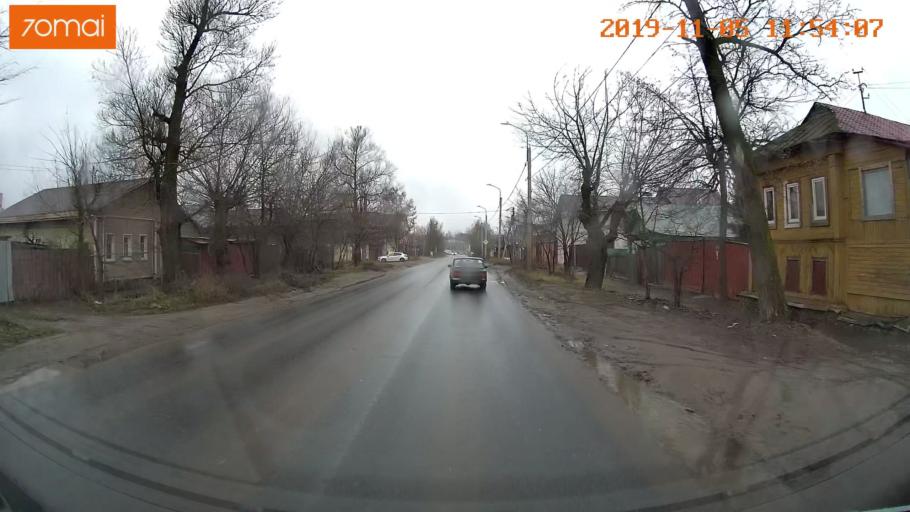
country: RU
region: Ivanovo
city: Bogorodskoye
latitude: 56.9927
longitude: 41.0309
